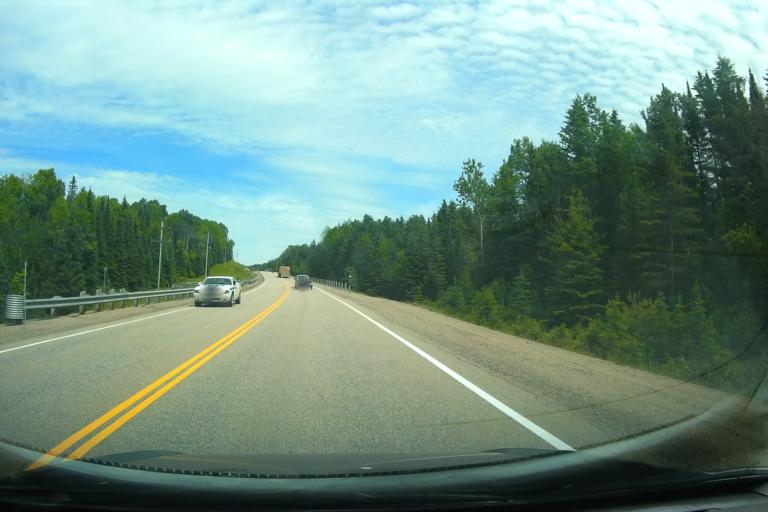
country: CA
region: Ontario
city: Mattawa
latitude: 46.2699
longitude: -79.0633
